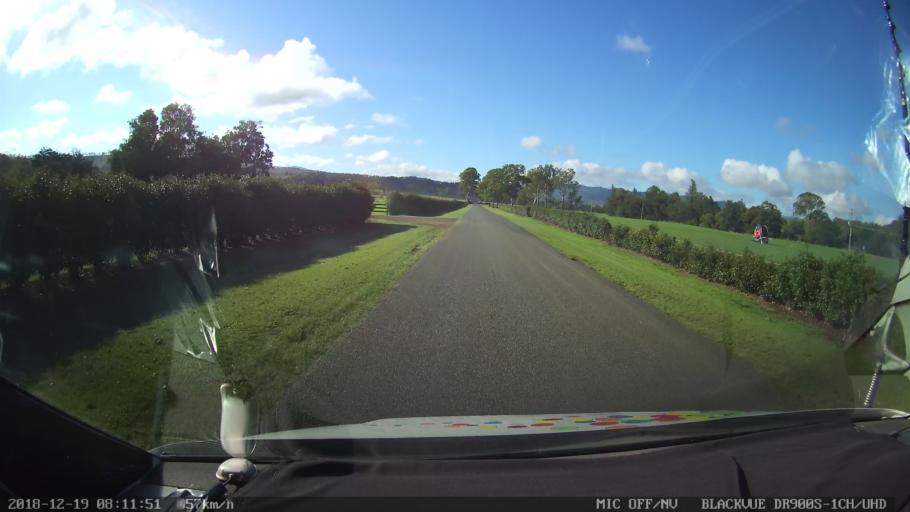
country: AU
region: Queensland
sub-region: Logan
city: Cedar Vale
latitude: -28.2219
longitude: 152.8916
